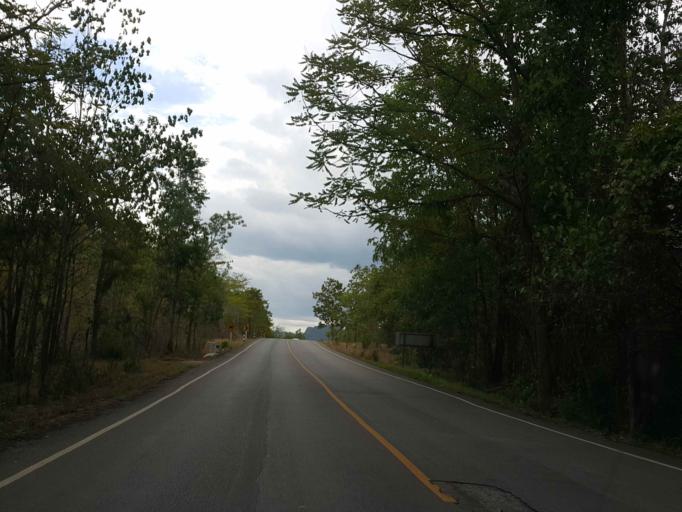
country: TH
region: Sukhothai
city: Thung Saliam
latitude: 17.3496
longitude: 99.4220
